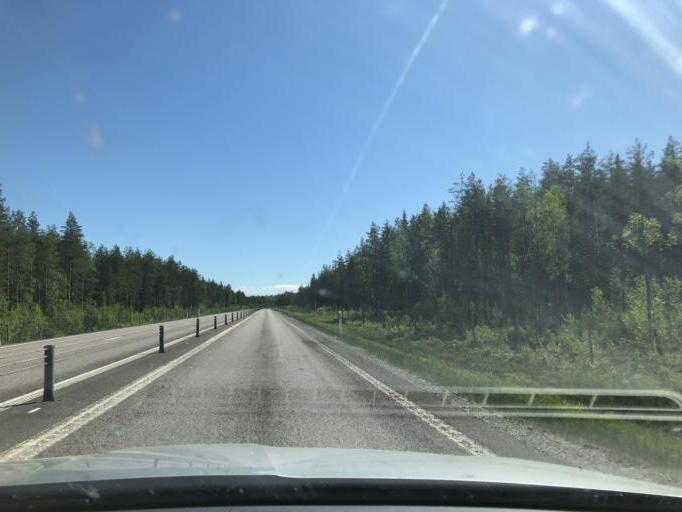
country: SE
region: Norrbotten
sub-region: Kalix Kommun
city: Toere
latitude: 65.9155
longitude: 22.7826
